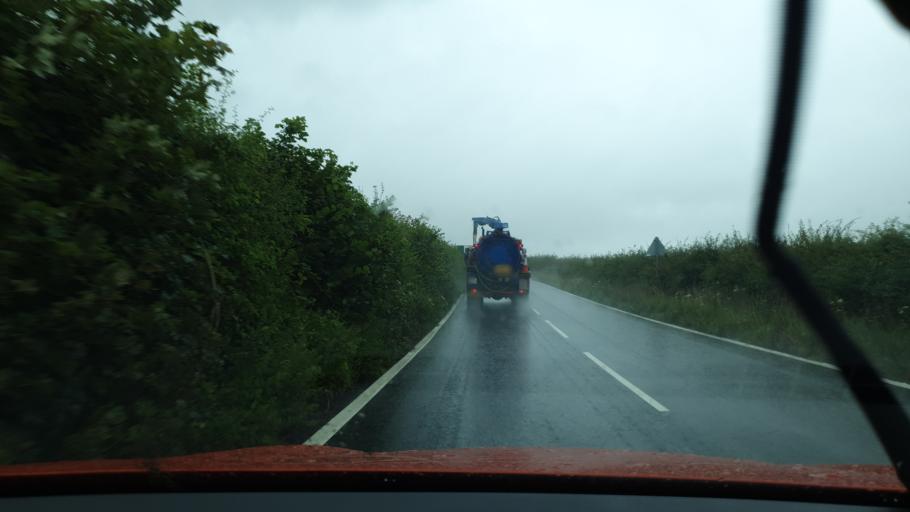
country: GB
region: England
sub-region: Cumbria
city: Millom
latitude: 54.2715
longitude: -3.2226
